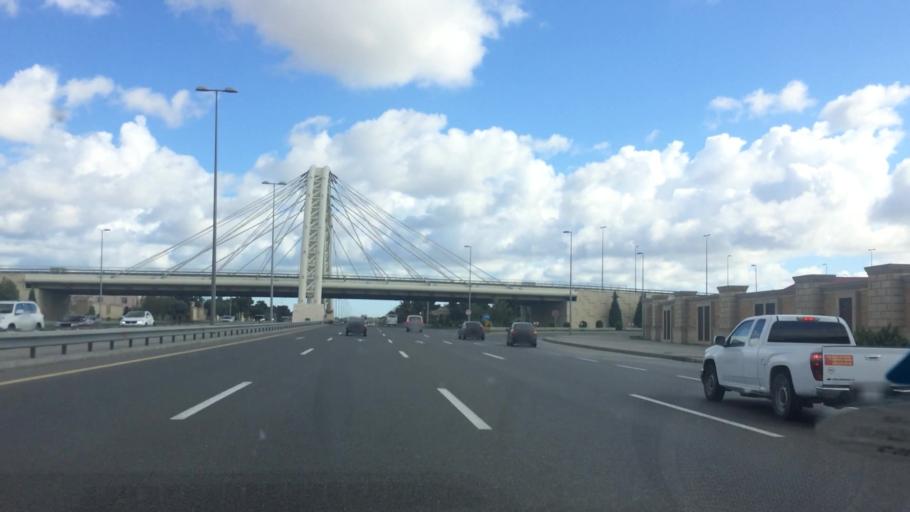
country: AZ
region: Baki
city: Biny Selo
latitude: 40.4585
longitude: 50.0742
